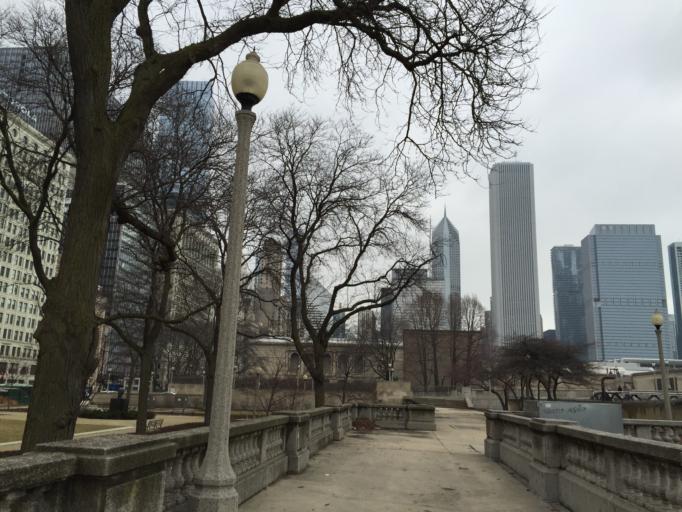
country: US
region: Illinois
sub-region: Cook County
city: Chicago
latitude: 41.8774
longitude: -87.6233
